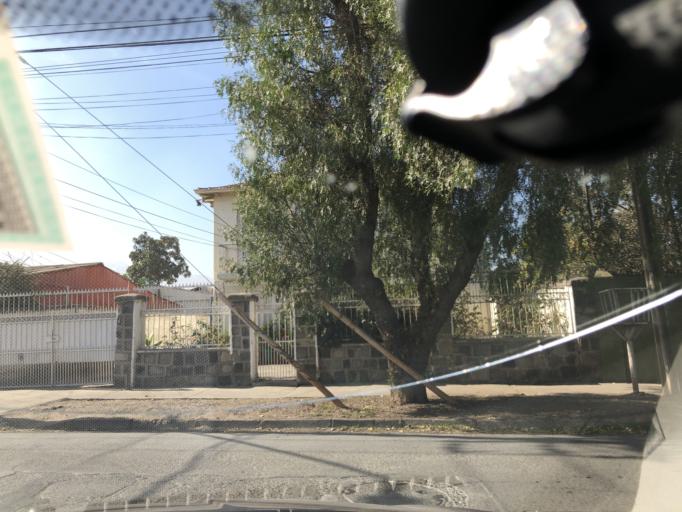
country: CL
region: Santiago Metropolitan
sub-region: Provincia de Cordillera
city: Puente Alto
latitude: -33.6155
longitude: -70.5684
